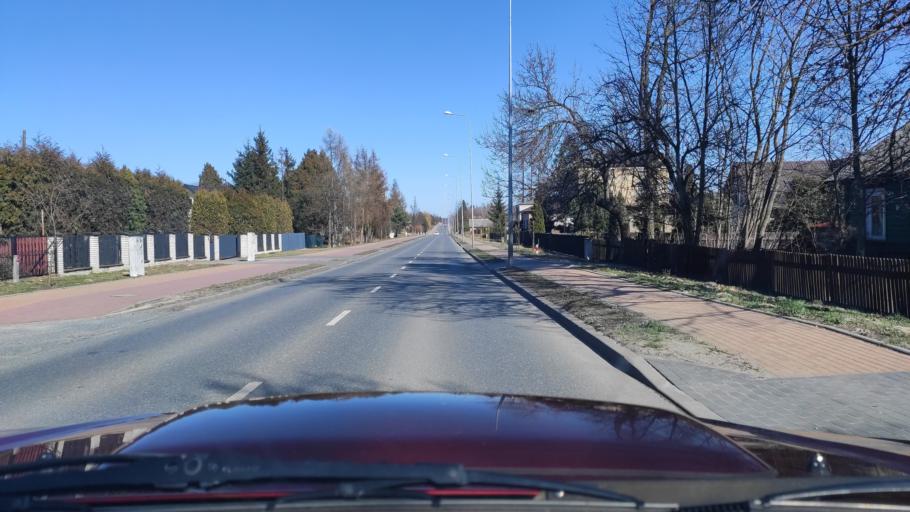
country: PL
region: Masovian Voivodeship
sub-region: Powiat zwolenski
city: Zwolen
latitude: 51.3623
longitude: 21.5833
